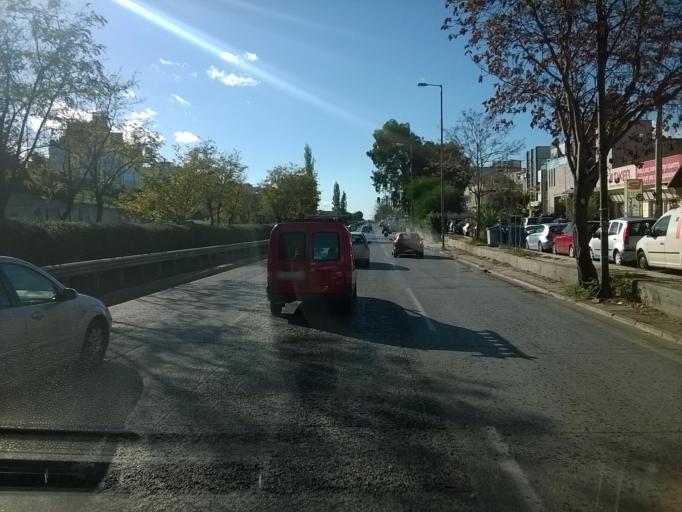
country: GR
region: Attica
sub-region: Nomarchia Athinas
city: Agios Dimitrios
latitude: 37.9286
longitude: 23.7443
